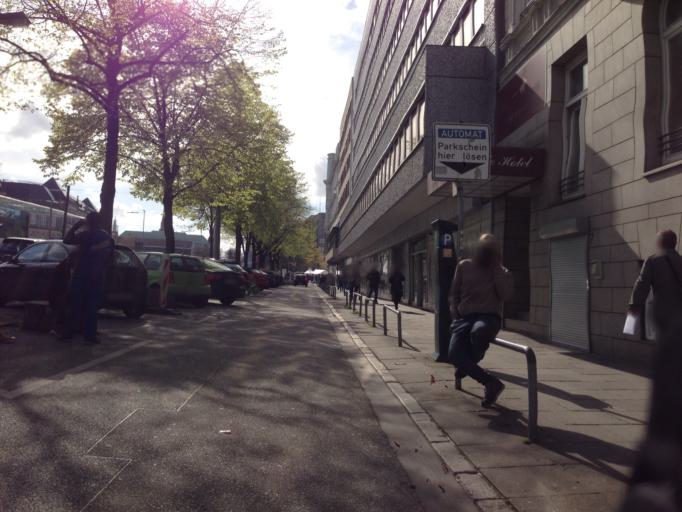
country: DE
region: Hamburg
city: St. Georg
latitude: 53.5526
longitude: 10.0122
